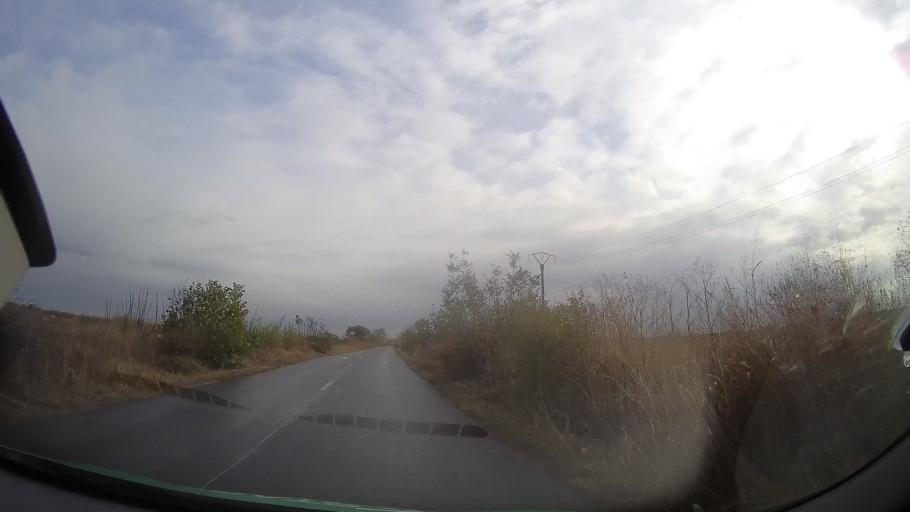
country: RO
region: Ialomita
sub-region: Comuna Maia
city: Maia
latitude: 44.7472
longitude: 26.3961
